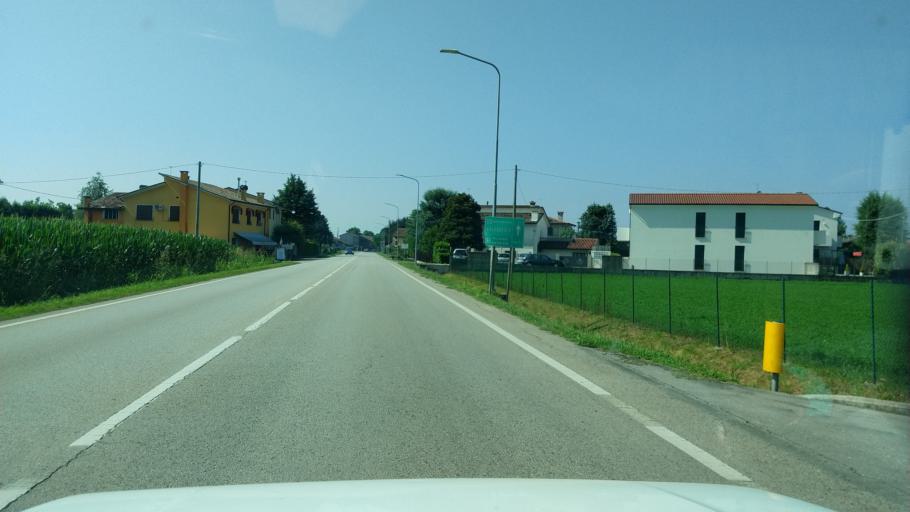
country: IT
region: Veneto
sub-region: Provincia di Vicenza
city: Bressanvido
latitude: 45.6670
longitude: 11.6356
